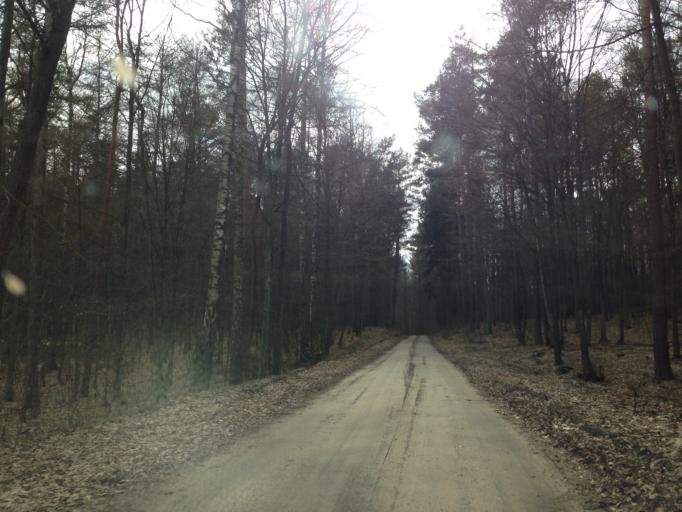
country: PL
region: Kujawsko-Pomorskie
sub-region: Powiat brodnicki
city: Gorzno
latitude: 53.2258
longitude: 19.7299
